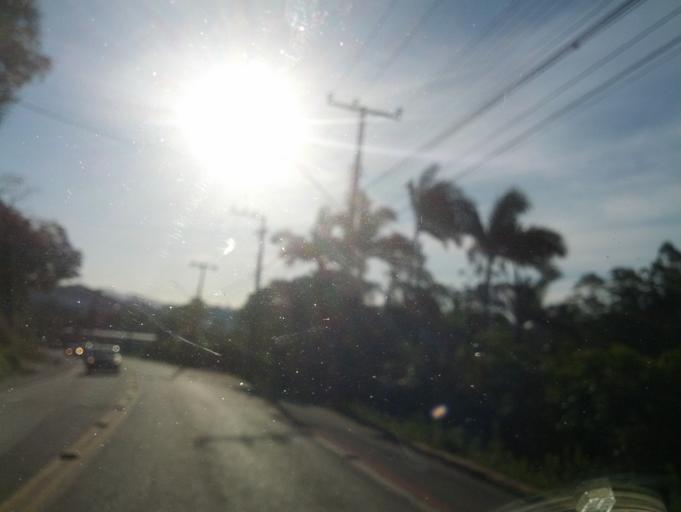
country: BR
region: Santa Catarina
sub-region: Indaial
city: Indaial
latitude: -26.8857
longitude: -49.1681
